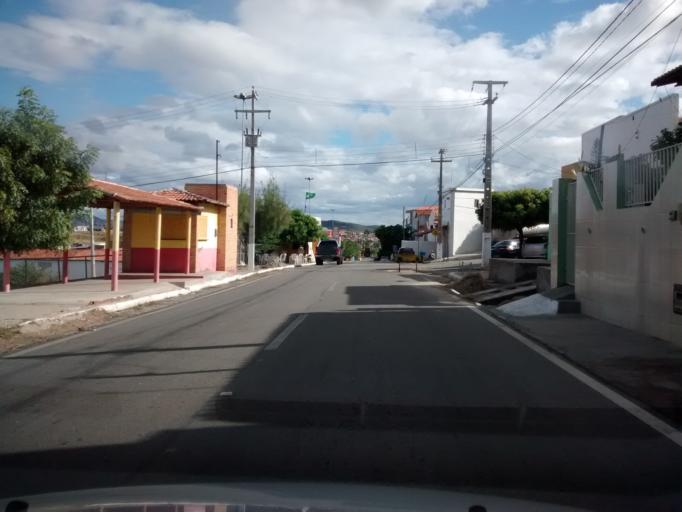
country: BR
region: Rio Grande do Norte
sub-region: Currais Novos
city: Currais Novos
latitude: -6.2659
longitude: -36.5204
